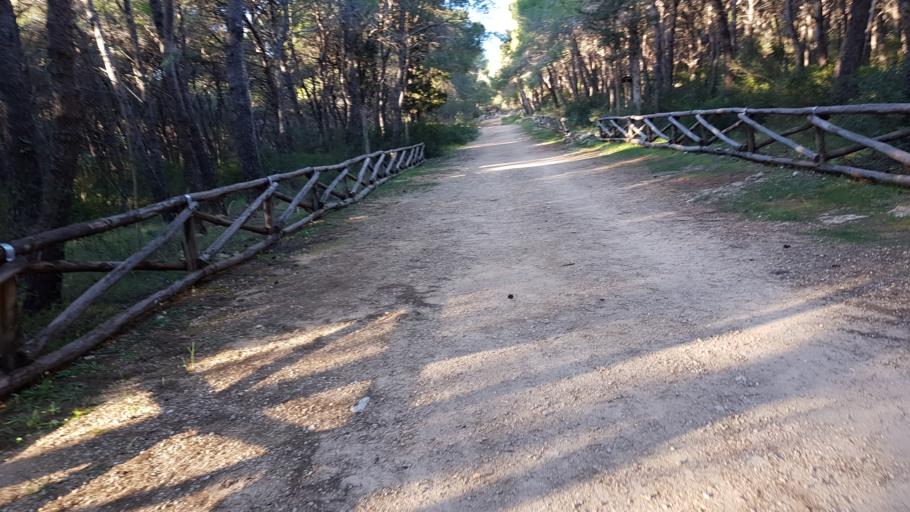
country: IT
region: Apulia
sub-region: Provincia di Lecce
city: Nardo
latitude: 40.1533
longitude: 17.9706
